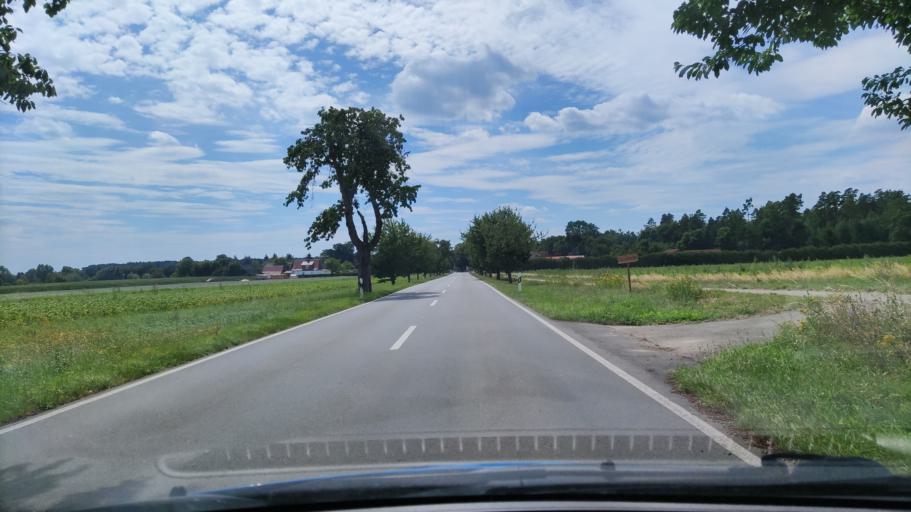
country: DE
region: Lower Saxony
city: Clenze
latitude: 52.9185
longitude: 10.9476
